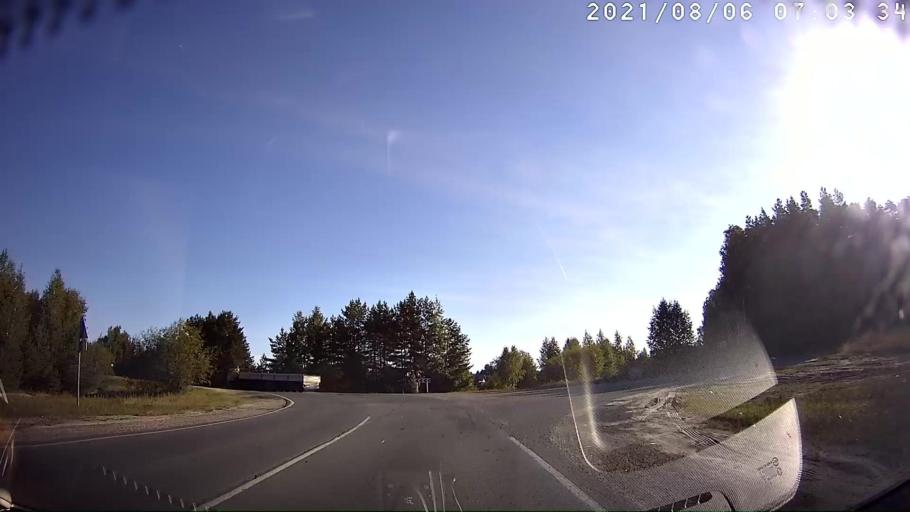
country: RU
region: Mariy-El
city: Yoshkar-Ola
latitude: 56.5417
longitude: 47.9825
